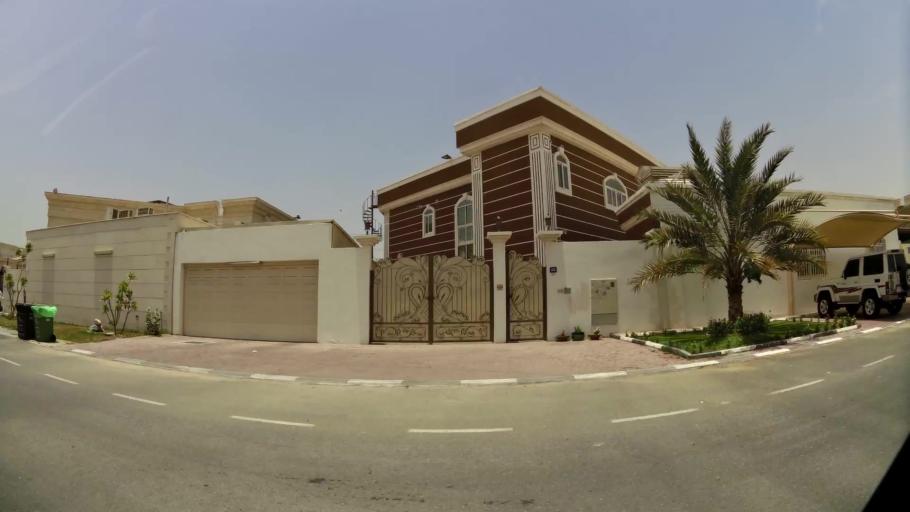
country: AE
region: Ash Shariqah
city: Sharjah
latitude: 25.2121
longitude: 55.3871
